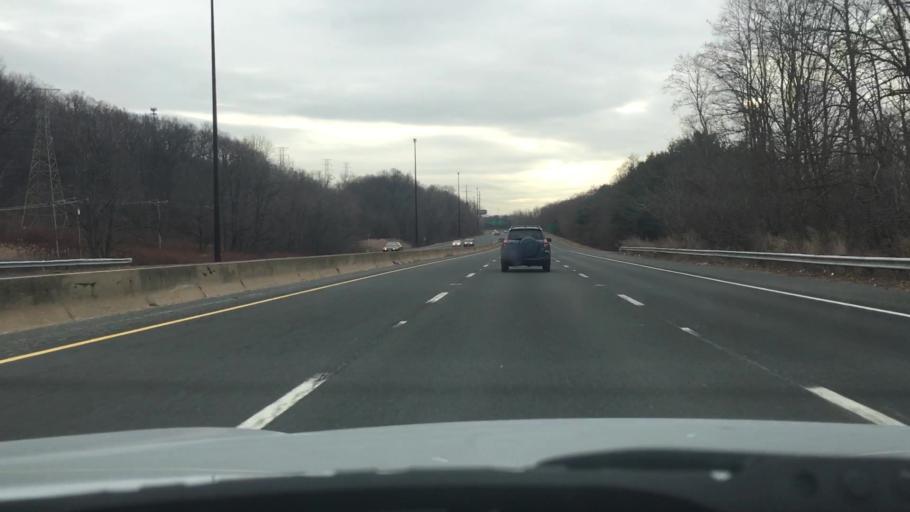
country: US
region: Massachusetts
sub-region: Hampden County
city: North Chicopee
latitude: 42.1685
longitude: -72.6106
